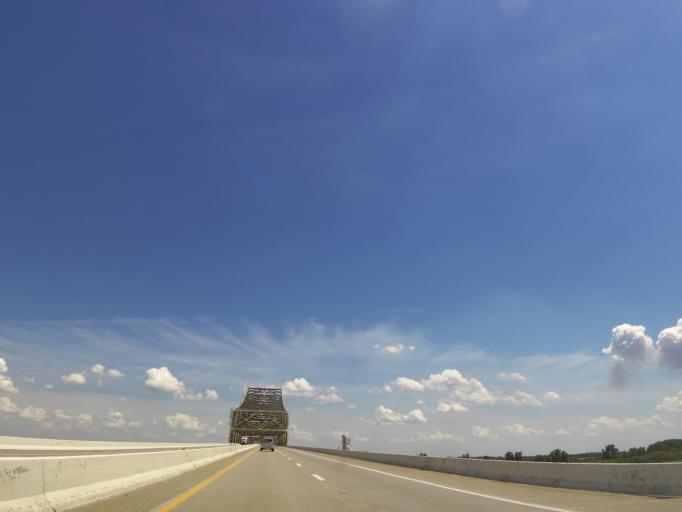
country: US
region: Missouri
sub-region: Pemiscot County
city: Caruthersville
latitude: 36.1172
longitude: -89.6141
